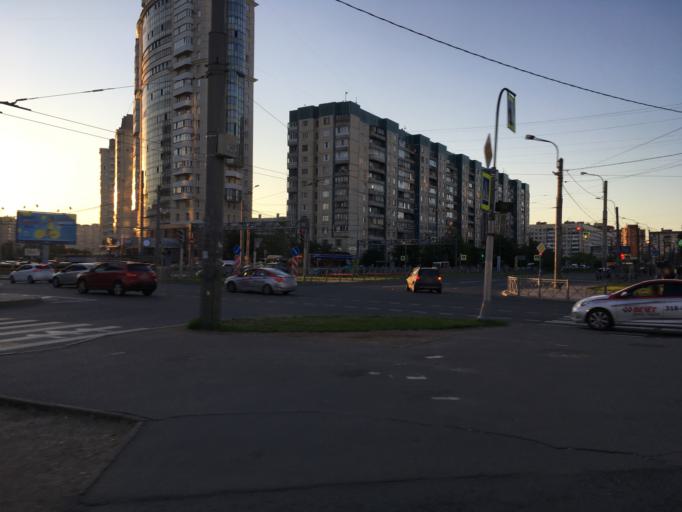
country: RU
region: St.-Petersburg
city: Komendantsky aerodrom
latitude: 60.0078
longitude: 30.2612
